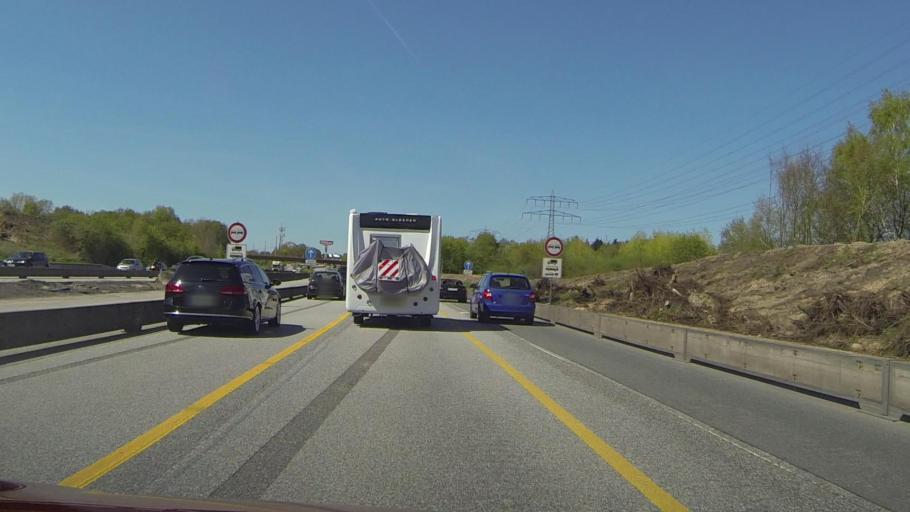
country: DE
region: Hamburg
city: Eidelstedt
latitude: 53.6103
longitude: 9.9173
